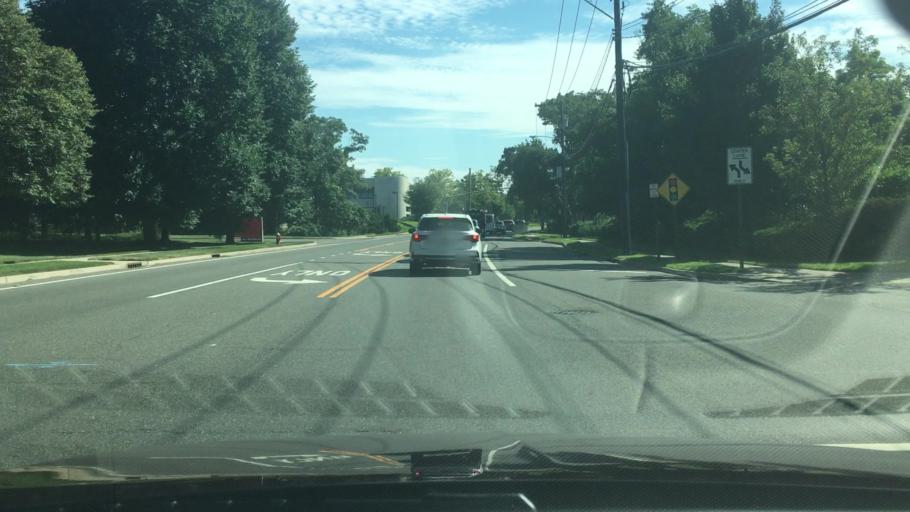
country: US
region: New York
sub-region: Suffolk County
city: Melville
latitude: 40.7760
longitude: -73.4255
